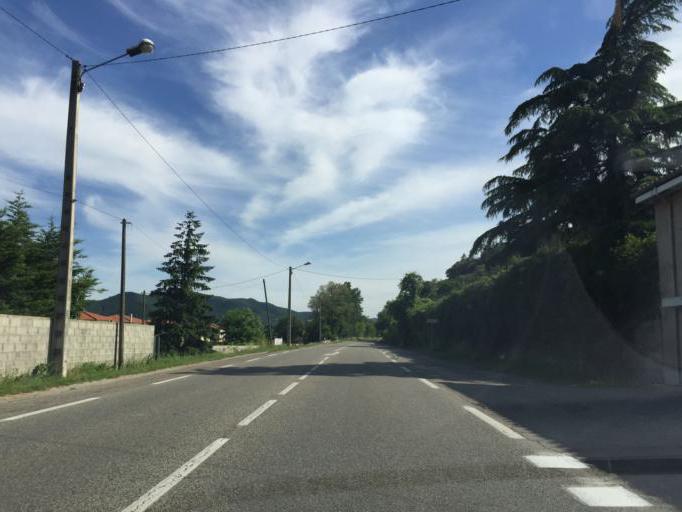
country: FR
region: Rhone-Alpes
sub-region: Departement de l'Ardeche
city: Le Pouzin
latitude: 44.7392
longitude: 4.7419
